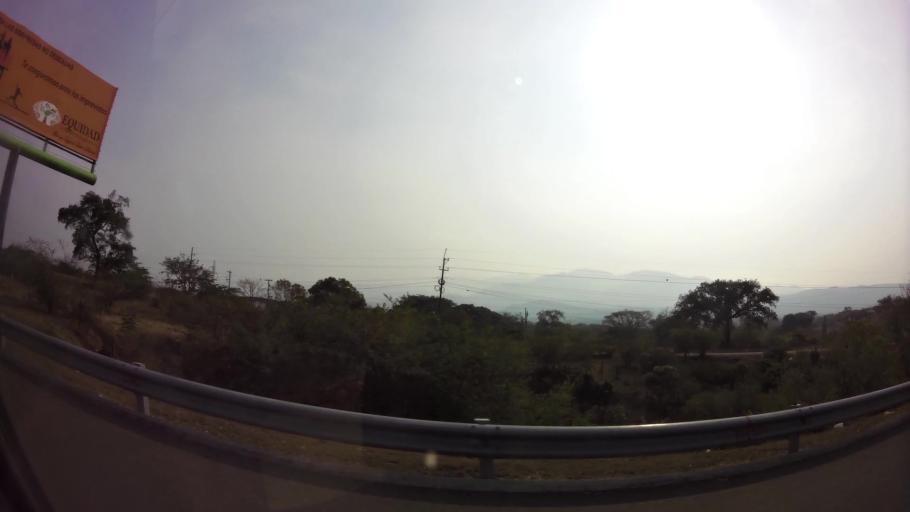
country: HN
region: Comayagua
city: Comayagua
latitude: 14.4208
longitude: -87.6277
